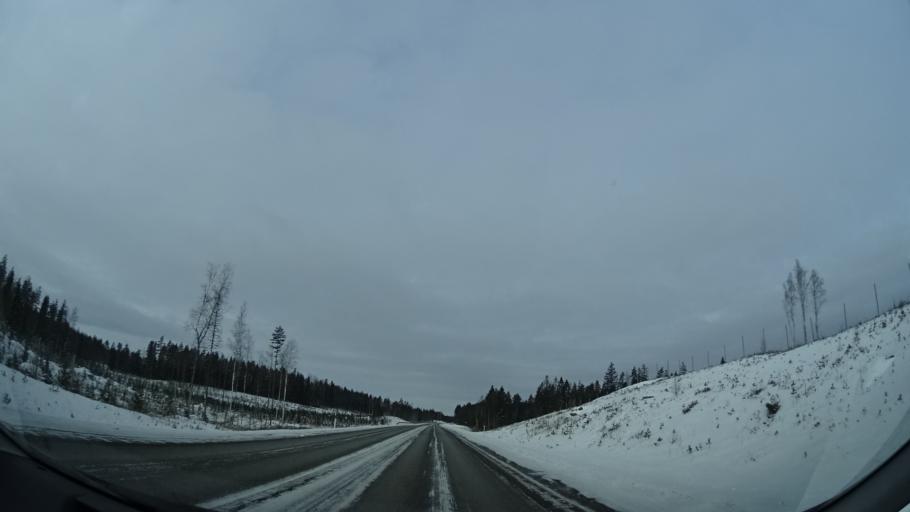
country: FI
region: Uusimaa
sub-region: Helsinki
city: Kaerkoelae
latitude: 60.6092
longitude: 24.0511
